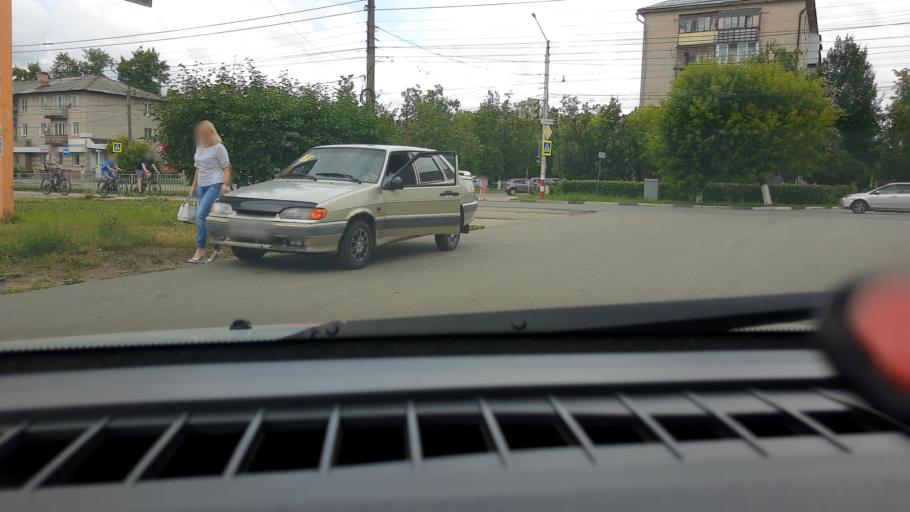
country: RU
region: Nizjnij Novgorod
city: Dzerzhinsk
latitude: 56.2338
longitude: 43.4452
